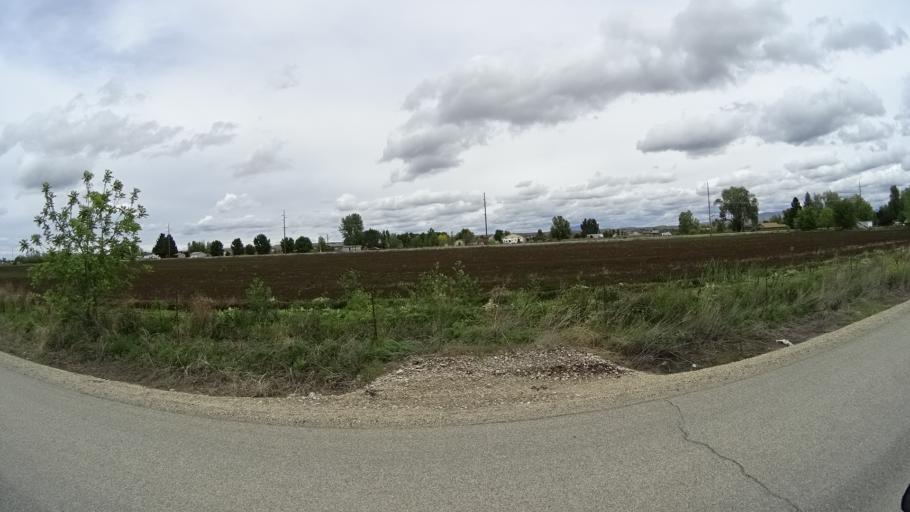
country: US
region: Idaho
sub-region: Ada County
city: Star
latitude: 43.6893
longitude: -116.4351
